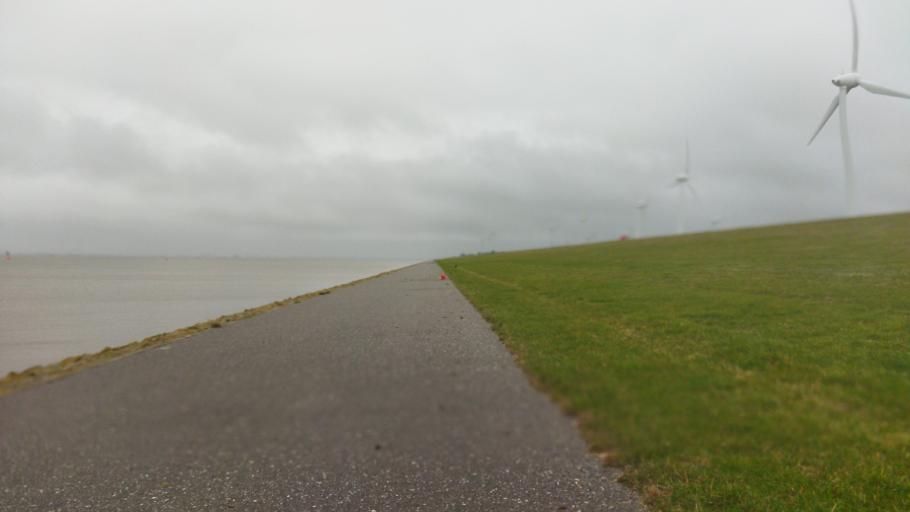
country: DE
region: Lower Saxony
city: Emden
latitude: 53.3350
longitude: 7.1155
